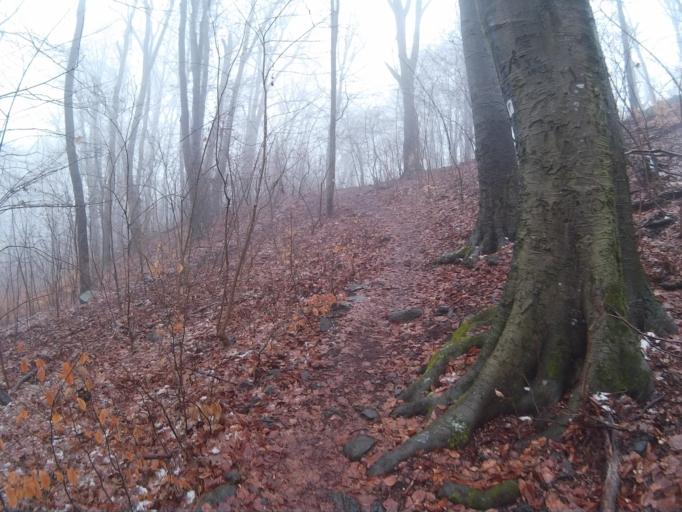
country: HU
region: Nograd
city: Somoskoujfalu
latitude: 48.1445
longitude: 19.8486
